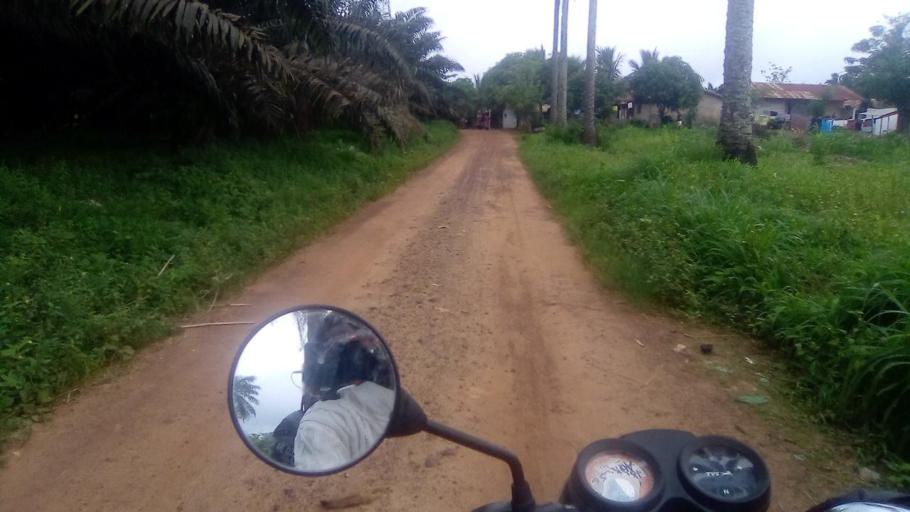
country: SL
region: Southern Province
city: Tongole
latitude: 7.4323
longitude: -11.8452
